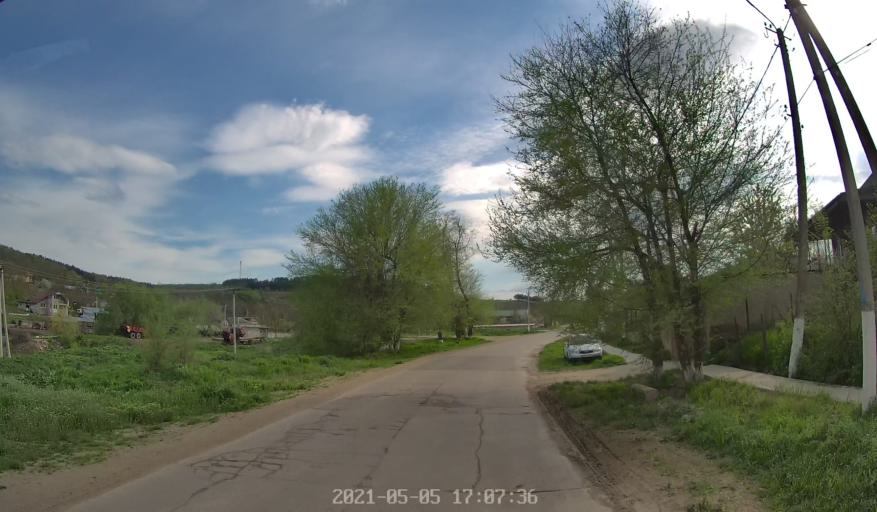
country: MD
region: Chisinau
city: Vadul lui Voda
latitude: 47.0116
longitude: 29.1334
